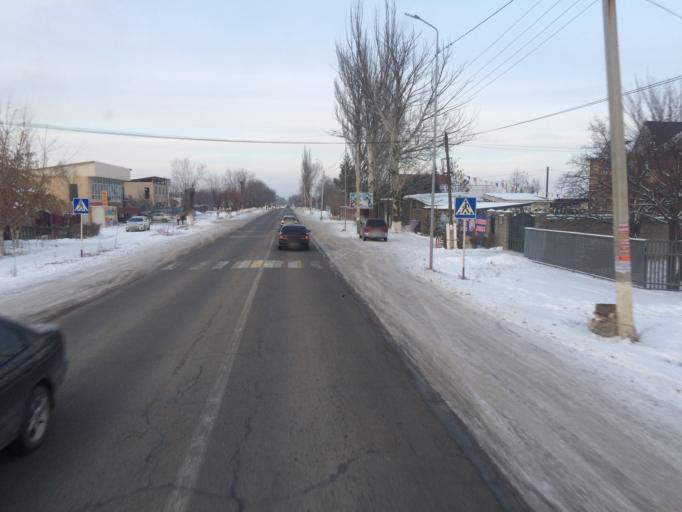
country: KZ
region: Almaty Oblysy
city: Burunday
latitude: 43.2678
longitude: 76.6704
